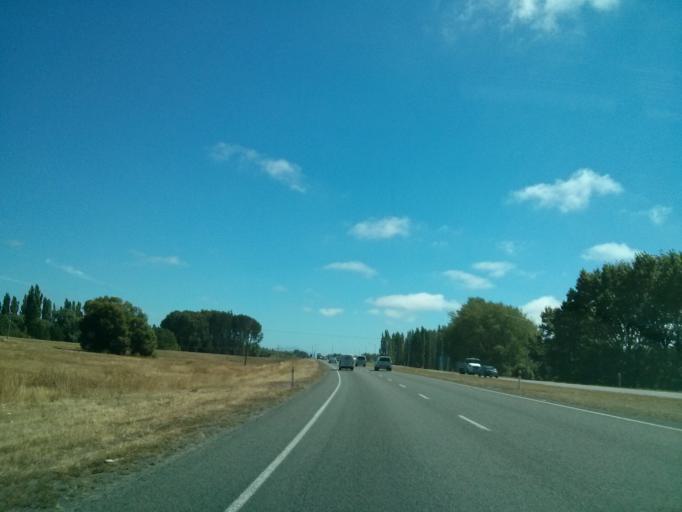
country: NZ
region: Canterbury
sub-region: Waimakariri District
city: Kaiapoi
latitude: -43.4215
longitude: 172.6484
